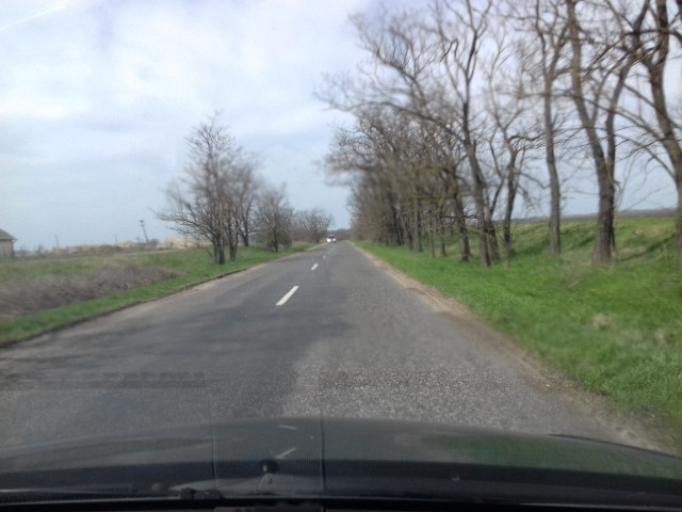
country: HU
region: Jasz-Nagykun-Szolnok
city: Cserkeszolo
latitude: 46.8865
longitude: 20.1434
